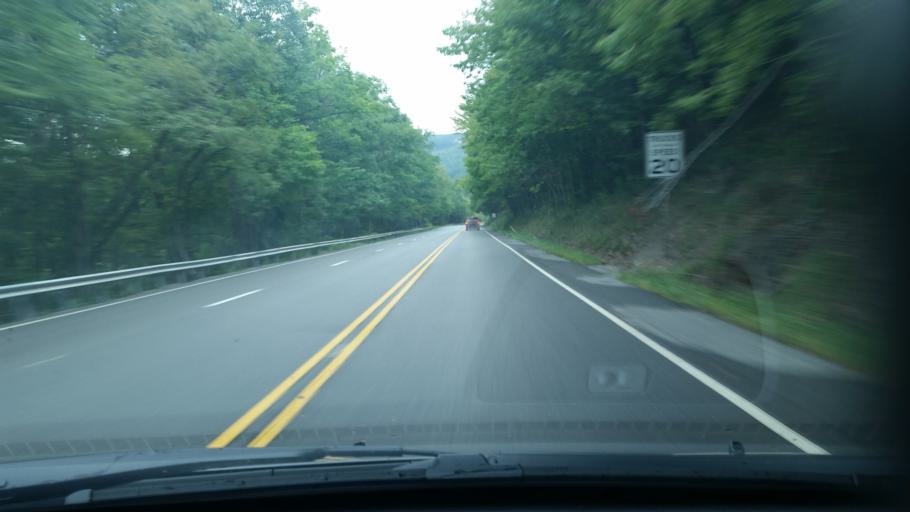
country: US
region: Pennsylvania
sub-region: Clearfield County
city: Shiloh
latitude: 41.0677
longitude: -78.3214
